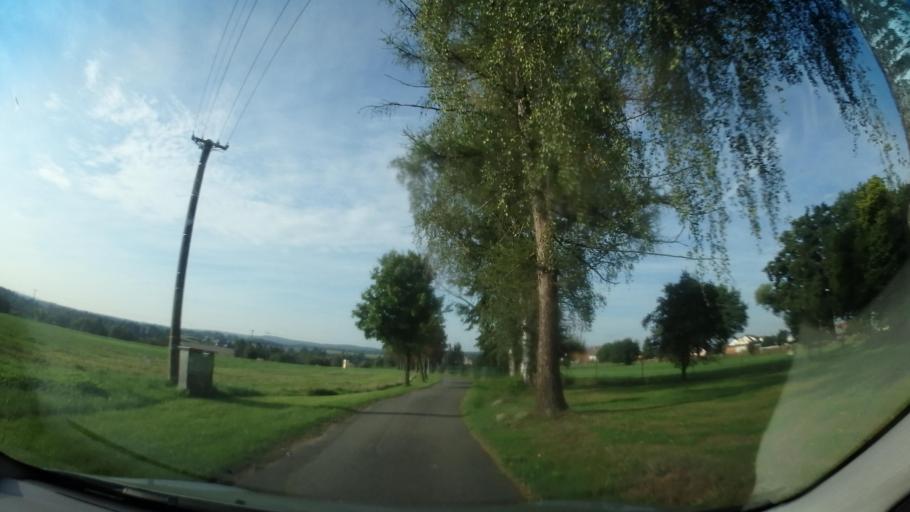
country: CZ
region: Jihocesky
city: Cimelice
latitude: 49.4236
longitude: 14.1215
